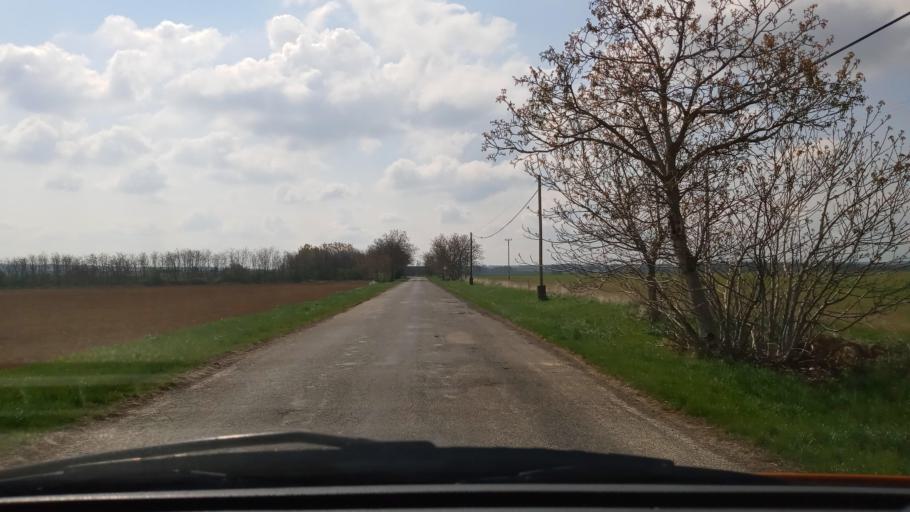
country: HU
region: Baranya
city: Pecsvarad
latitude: 46.0863
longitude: 18.5050
